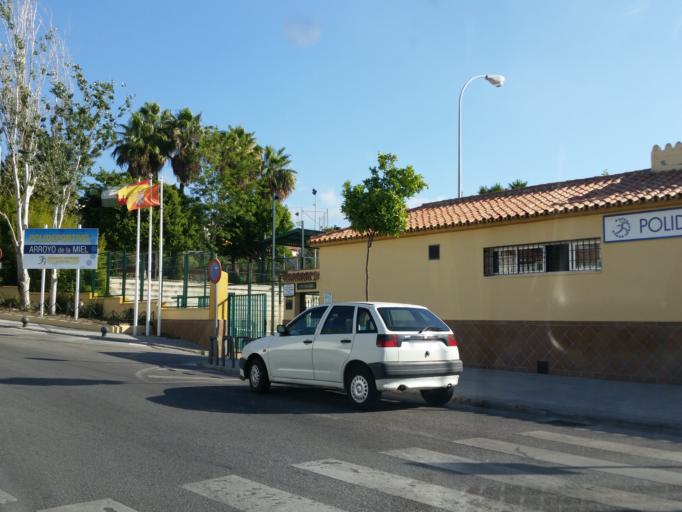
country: ES
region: Andalusia
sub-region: Provincia de Malaga
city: Torremolinos
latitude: 36.6040
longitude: -4.5328
